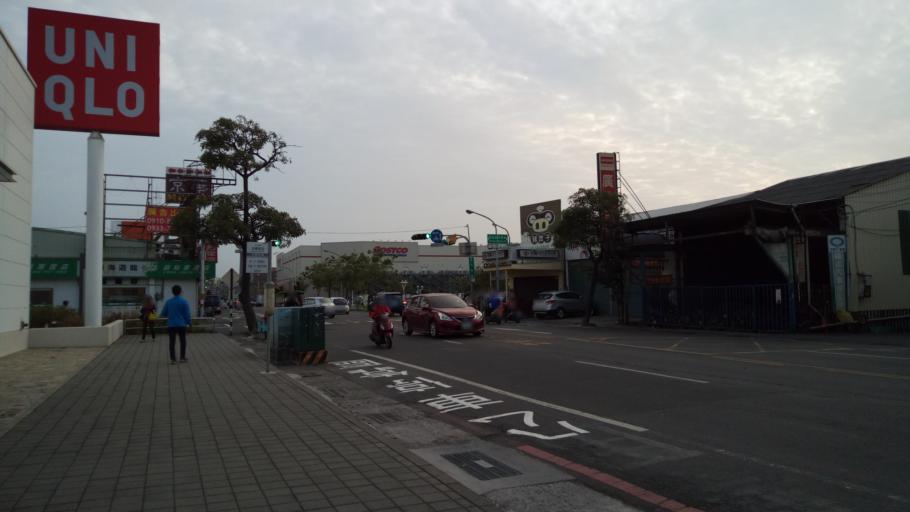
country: TW
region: Taiwan
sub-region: Tainan
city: Tainan
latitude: 23.0125
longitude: 120.1940
